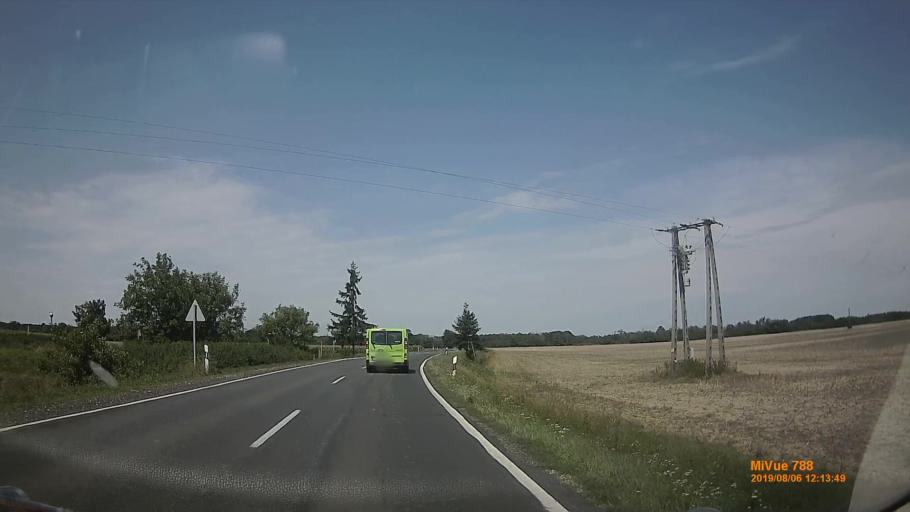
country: HU
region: Vas
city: Vasvar
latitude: 47.1342
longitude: 16.8370
